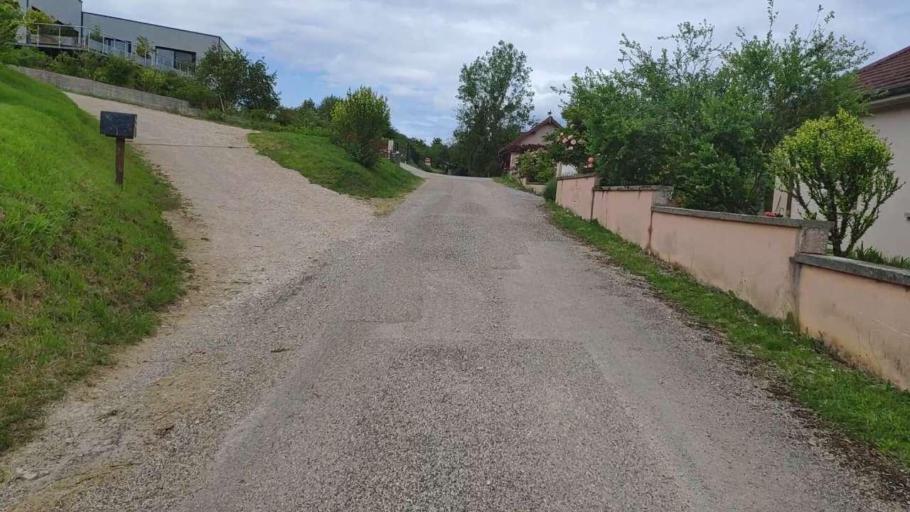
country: FR
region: Franche-Comte
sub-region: Departement du Jura
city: Perrigny
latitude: 46.7862
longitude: 5.5795
